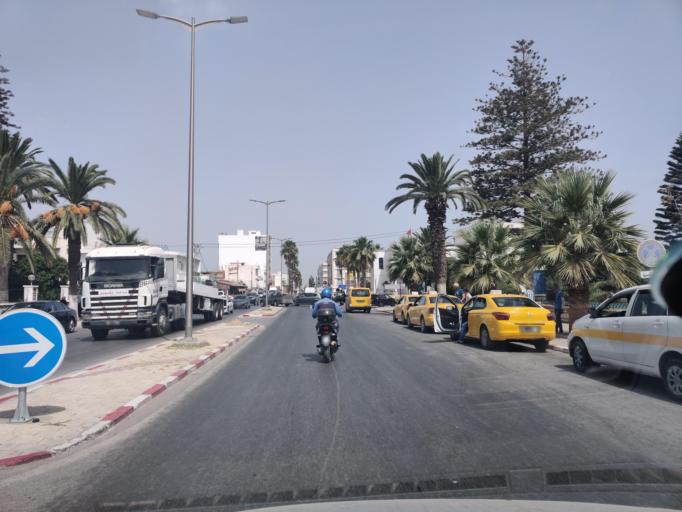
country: TN
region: Nabul
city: Bu `Urqub
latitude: 36.5972
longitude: 10.4999
